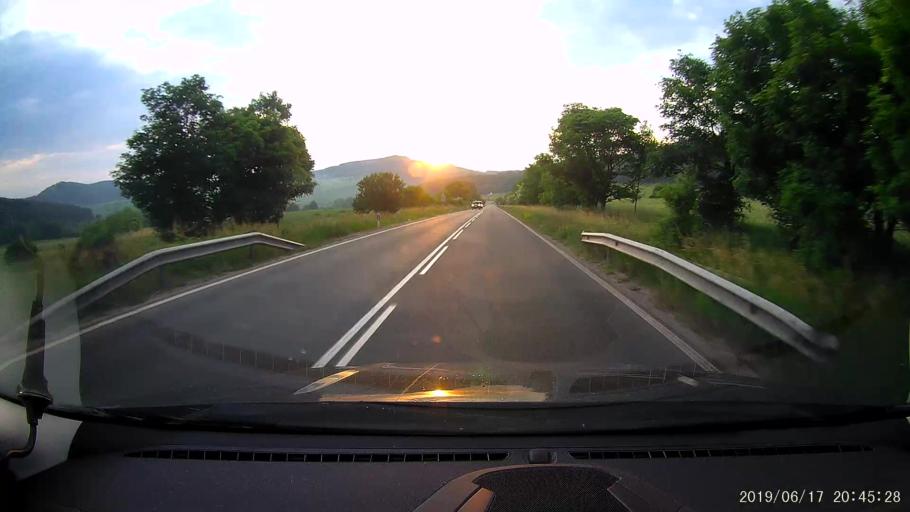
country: BG
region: Sofiya
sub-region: Obshtina Dragoman
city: Dragoman
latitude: 42.9337
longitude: 22.9197
